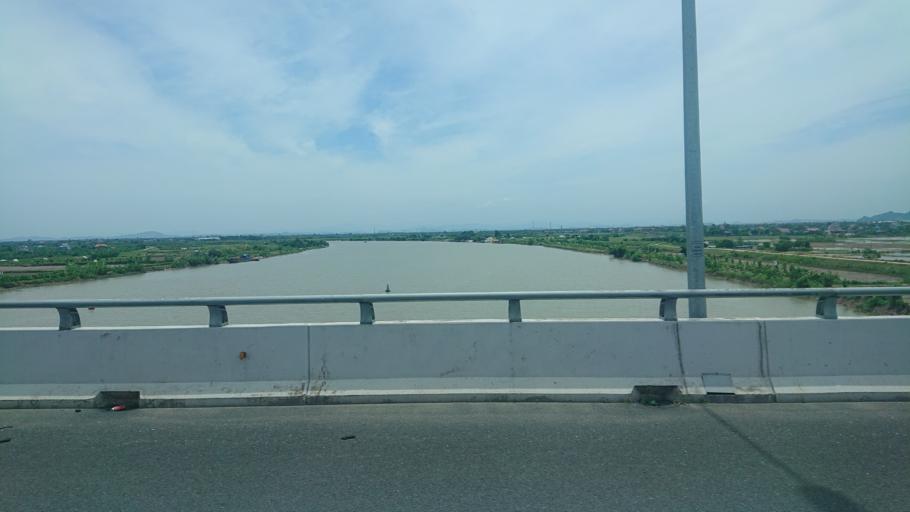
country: VN
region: Hai Phong
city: An Lao
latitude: 20.8075
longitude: 106.5136
